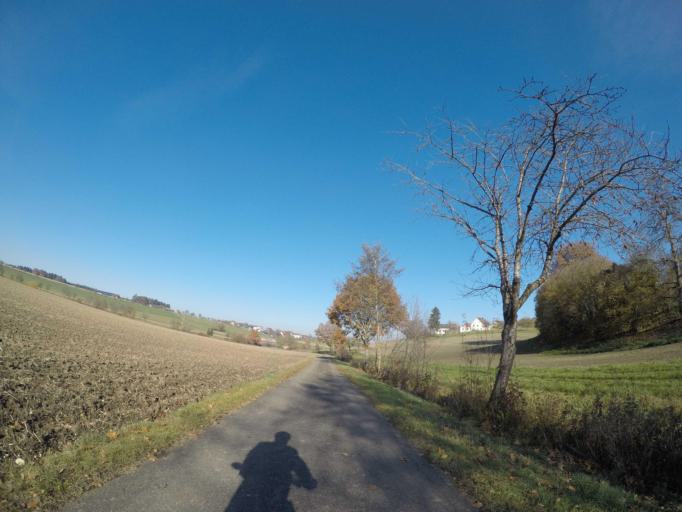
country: DE
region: Baden-Wuerttemberg
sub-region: Tuebingen Region
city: Hausen am Bussen
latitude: 48.2180
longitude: 9.6086
